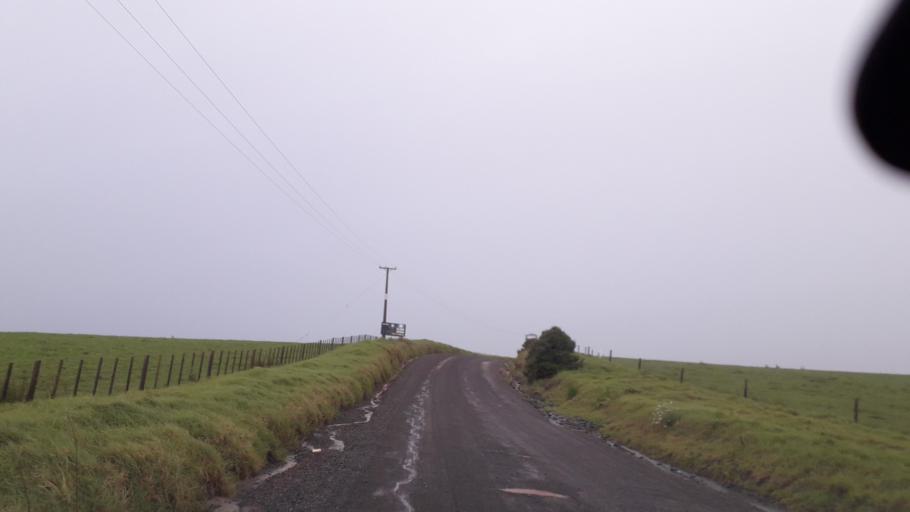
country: NZ
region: Northland
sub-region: Far North District
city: Kerikeri
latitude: -35.1309
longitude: 174.0037
